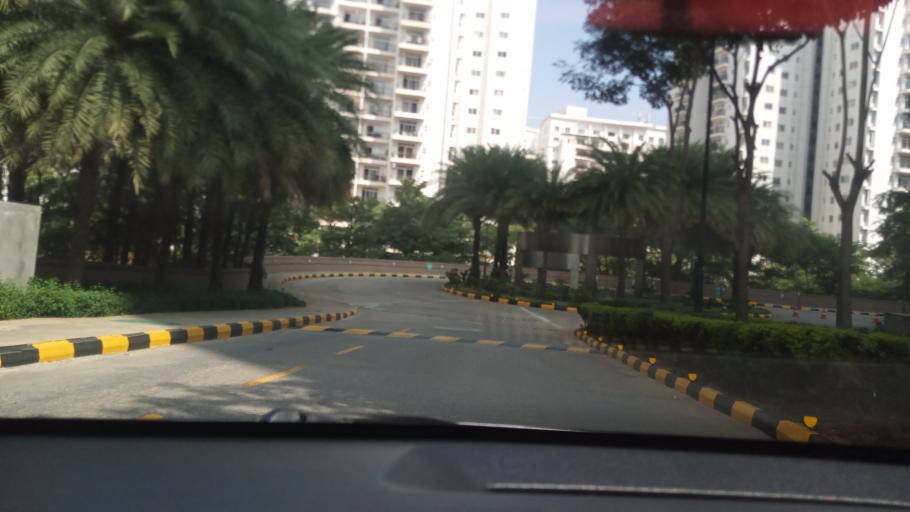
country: IN
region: Karnataka
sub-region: Bangalore Rural
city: Hoskote
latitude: 12.9914
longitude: 77.7290
